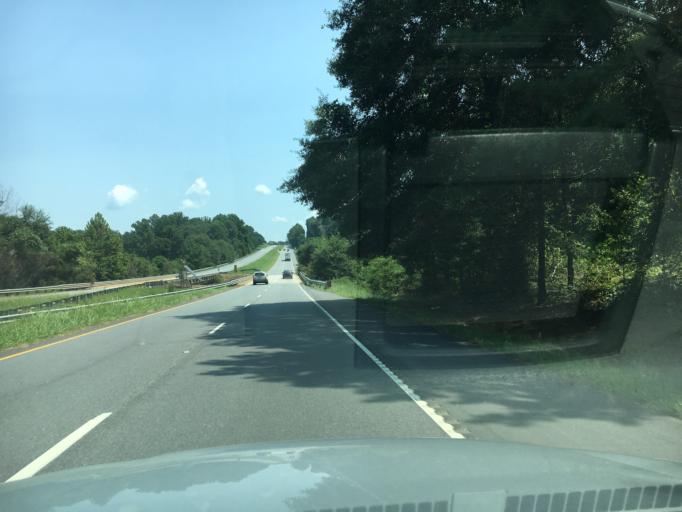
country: US
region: South Carolina
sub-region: Anderson County
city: Pendleton
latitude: 34.6455
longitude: -82.8019
